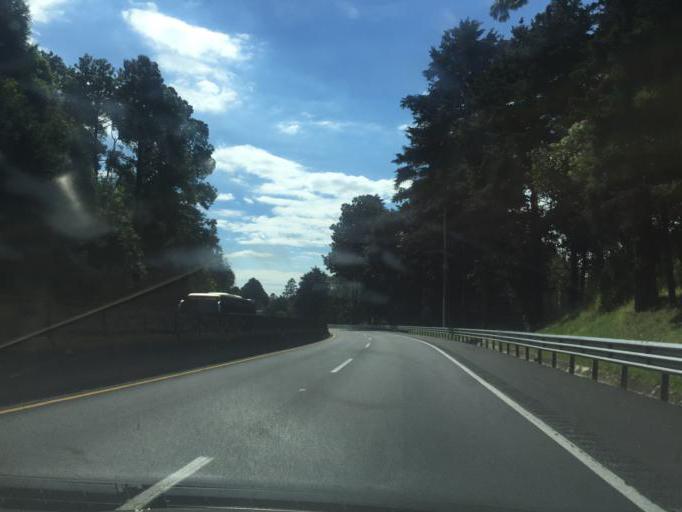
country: MX
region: Morelos
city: Tres Marias
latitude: 19.0367
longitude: -99.2279
